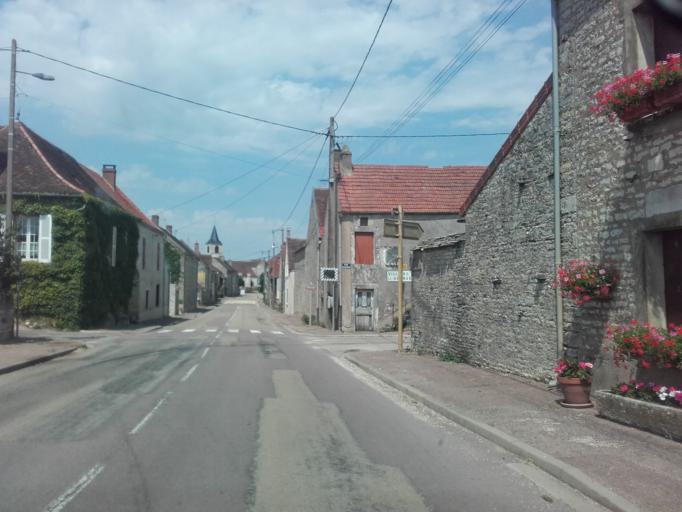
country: FR
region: Bourgogne
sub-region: Departement de l'Yonne
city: Joux-la-Ville
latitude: 47.6699
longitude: 3.8783
